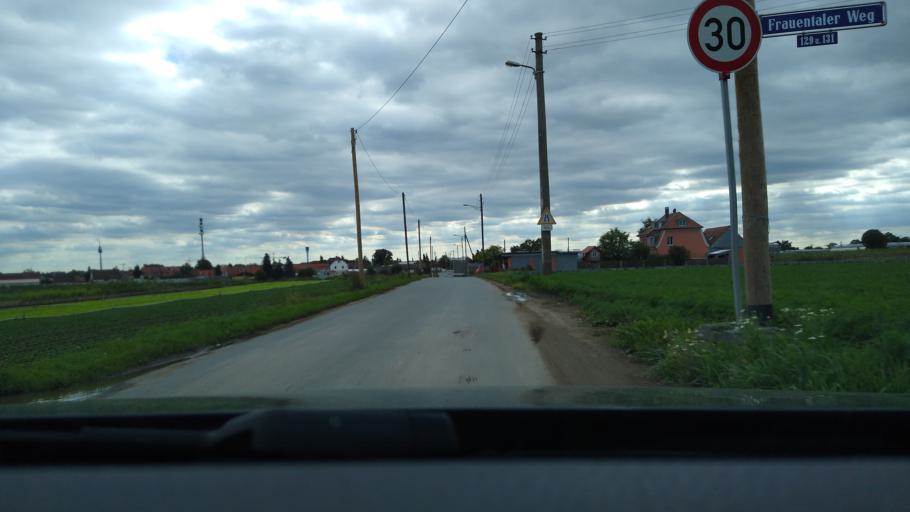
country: DE
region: Bavaria
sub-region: Regierungsbezirk Mittelfranken
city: Wetzendorf
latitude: 49.4771
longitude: 11.0395
